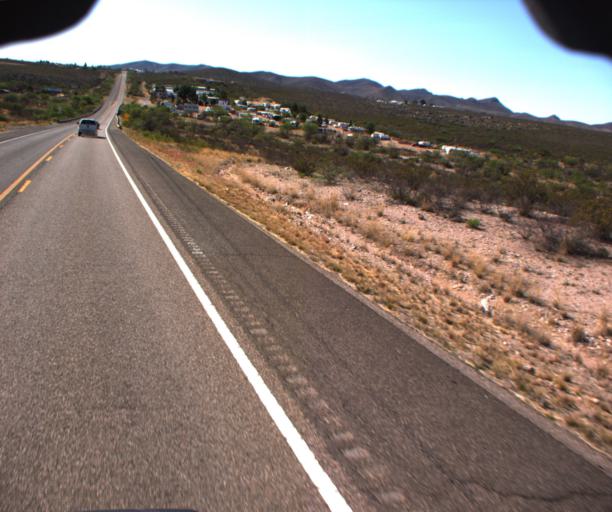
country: US
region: Arizona
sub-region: Cochise County
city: Tombstone
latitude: 31.7342
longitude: -110.0823
